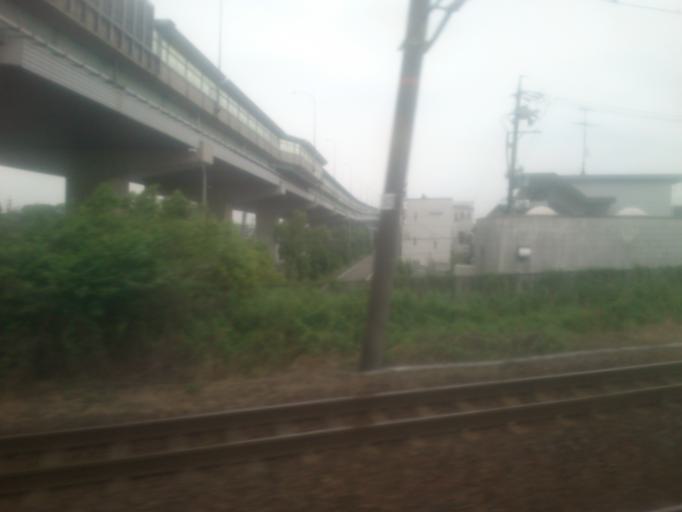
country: JP
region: Aichi
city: Inazawa
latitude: 35.2195
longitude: 136.8395
